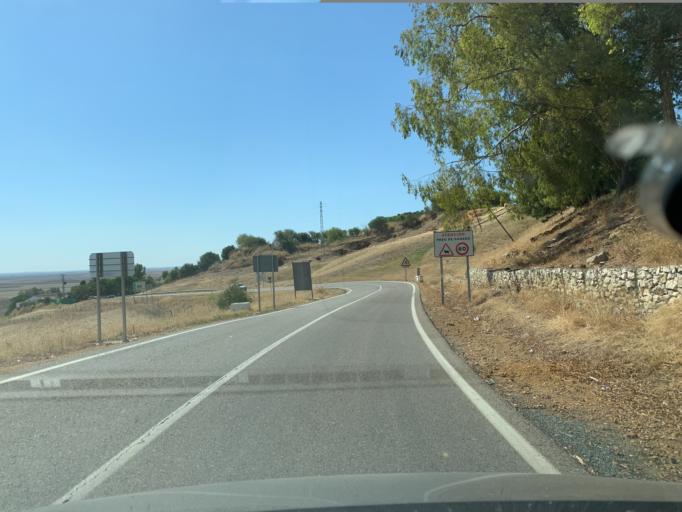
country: ES
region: Andalusia
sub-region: Provincia de Sevilla
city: Carmona
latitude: 37.4679
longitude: -5.6333
